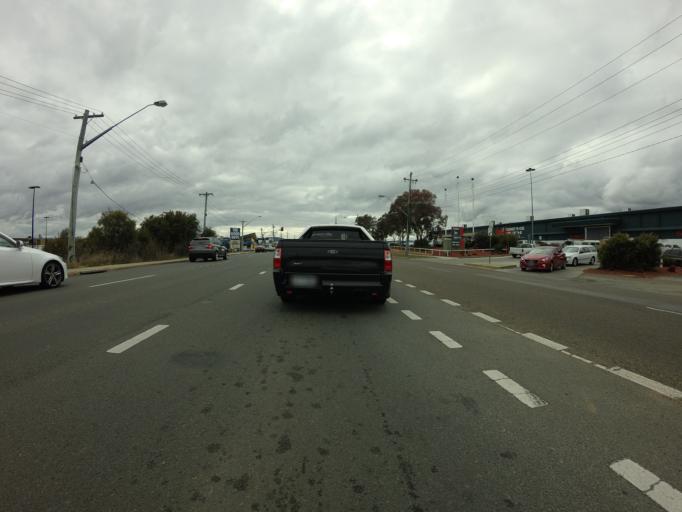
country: AU
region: Australian Capital Territory
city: Forrest
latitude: -35.3318
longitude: 149.1779
